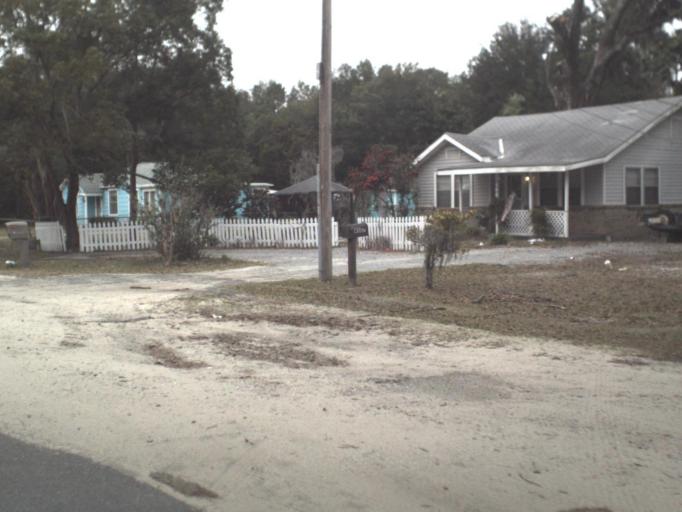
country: US
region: Florida
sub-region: Bay County
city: Parker
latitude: 30.1311
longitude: -85.6107
